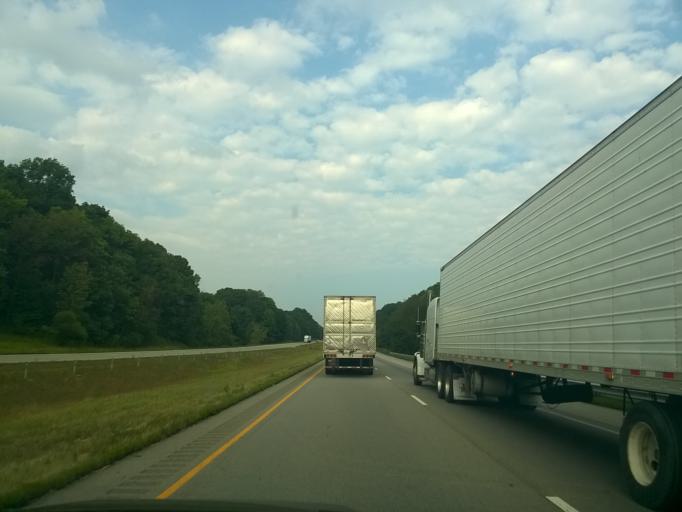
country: US
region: Indiana
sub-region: Putnam County
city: Cloverdale
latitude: 39.5072
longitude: -86.9422
